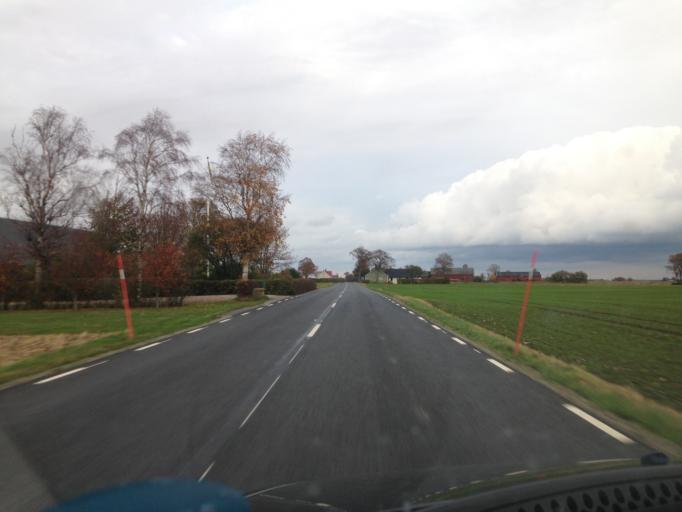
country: SE
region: Skane
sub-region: Ystads Kommun
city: Kopingebro
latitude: 55.4283
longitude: 14.1597
